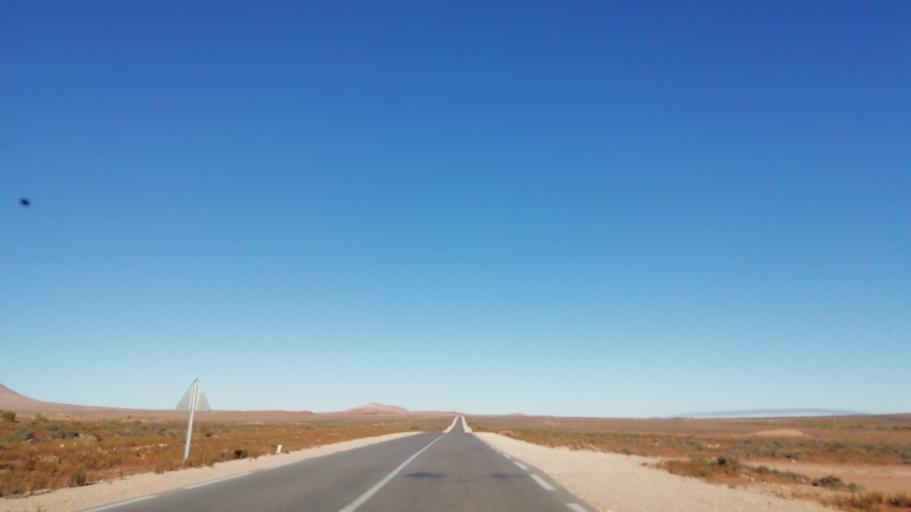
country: DZ
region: El Bayadh
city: El Abiodh Sidi Cheikh
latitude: 33.0961
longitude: 0.2030
